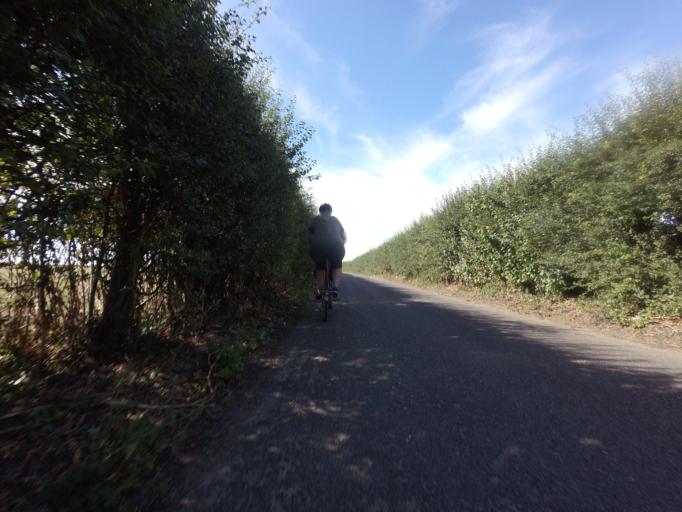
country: GB
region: England
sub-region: Kent
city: Birchington-on-Sea
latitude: 51.3463
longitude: 1.2612
